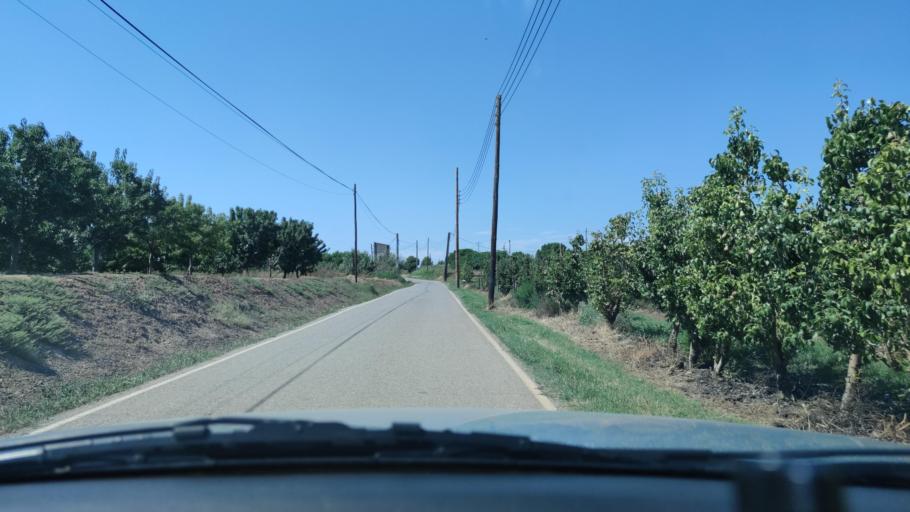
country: ES
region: Catalonia
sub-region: Provincia de Lleida
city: Torrefarrera
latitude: 41.6605
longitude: 0.6206
